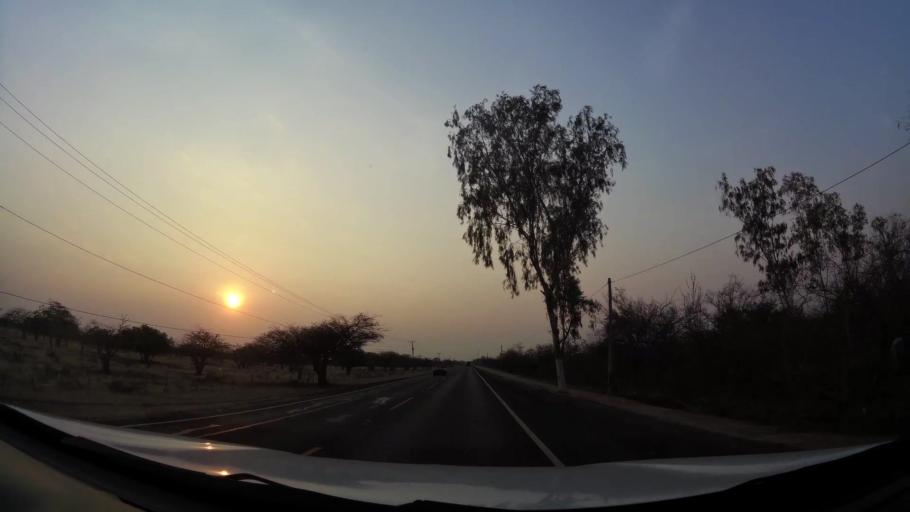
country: NI
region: Leon
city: La Paz Centro
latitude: 12.2850
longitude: -86.7554
